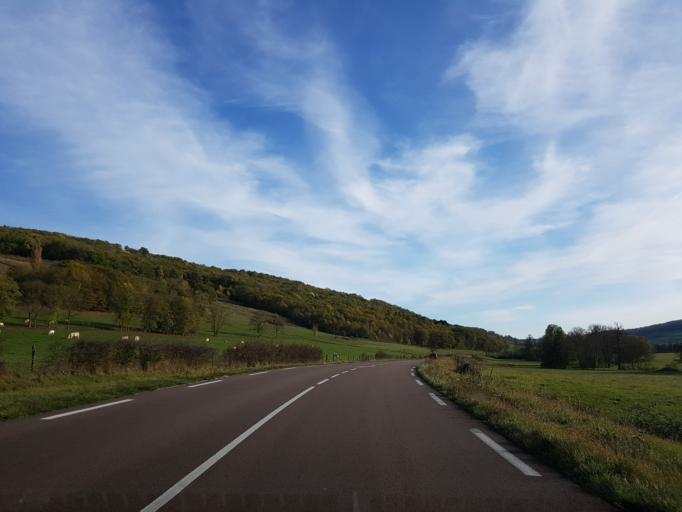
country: FR
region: Bourgogne
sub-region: Departement de la Cote-d'Or
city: Vitteaux
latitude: 47.3811
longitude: 4.5595
